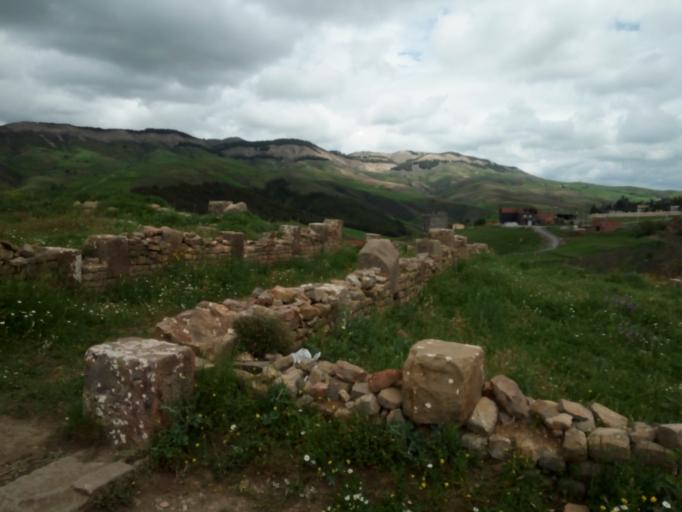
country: DZ
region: Setif
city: El Eulma
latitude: 36.3193
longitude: 5.7377
